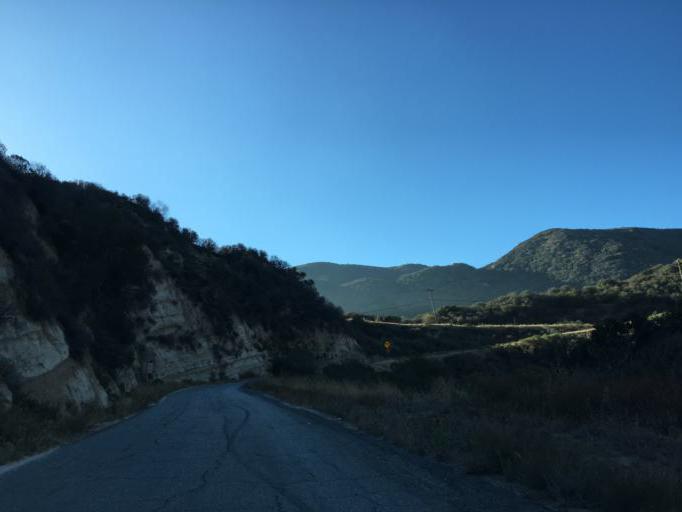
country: US
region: California
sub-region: Los Angeles County
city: San Fernando
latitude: 34.3199
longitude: -118.3385
